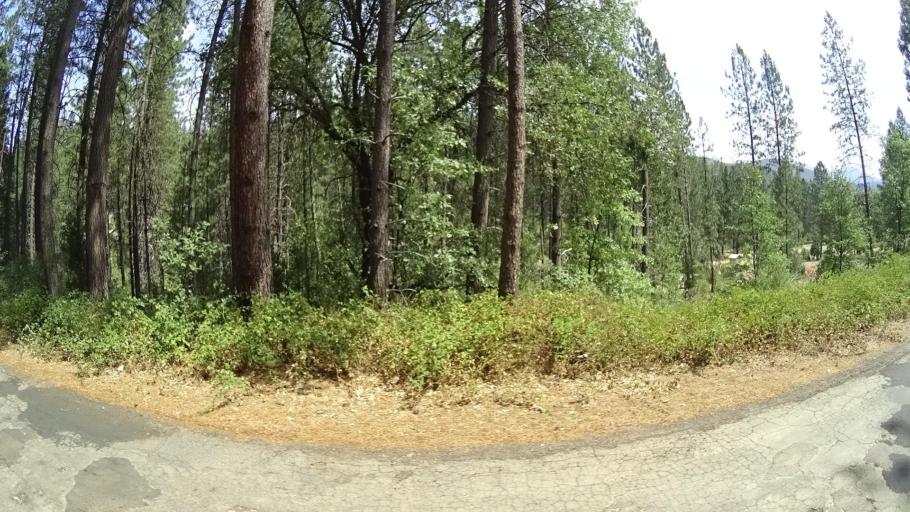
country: US
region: California
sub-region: Mariposa County
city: Midpines
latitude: 37.7515
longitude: -120.0477
